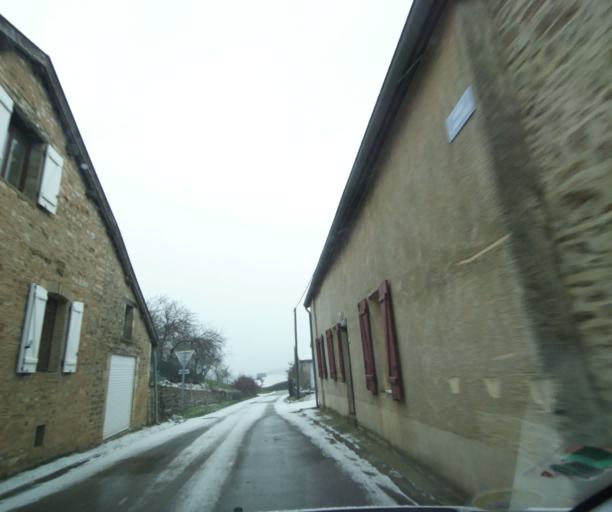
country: FR
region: Champagne-Ardenne
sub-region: Departement de la Haute-Marne
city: Wassy
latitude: 48.4748
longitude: 5.0358
